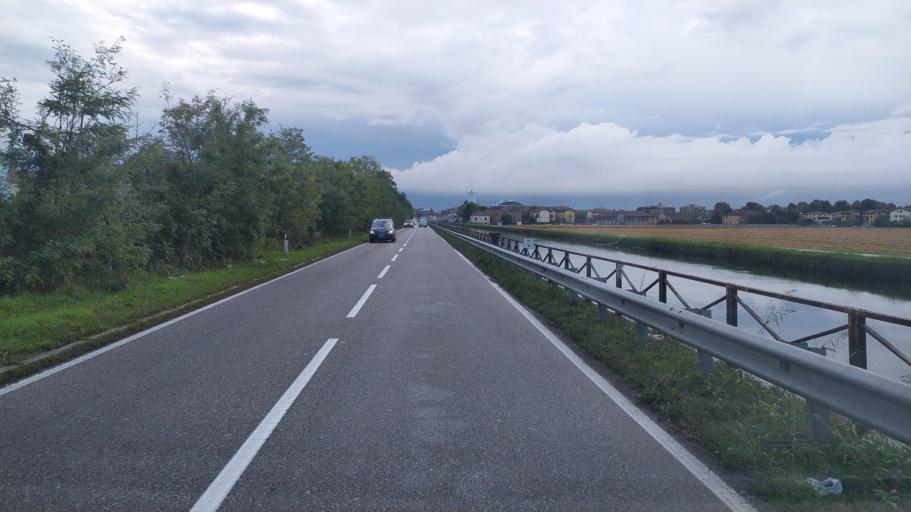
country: IT
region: Lombardy
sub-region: Citta metropolitana di Milano
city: Gaggiano
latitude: 45.4059
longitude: 9.0245
